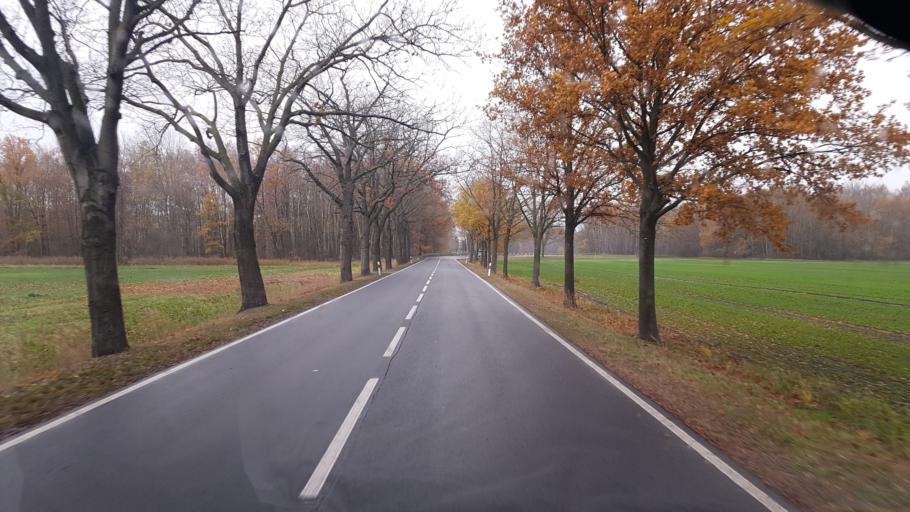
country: DE
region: Brandenburg
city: Schraden
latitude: 51.4461
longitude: 13.7109
